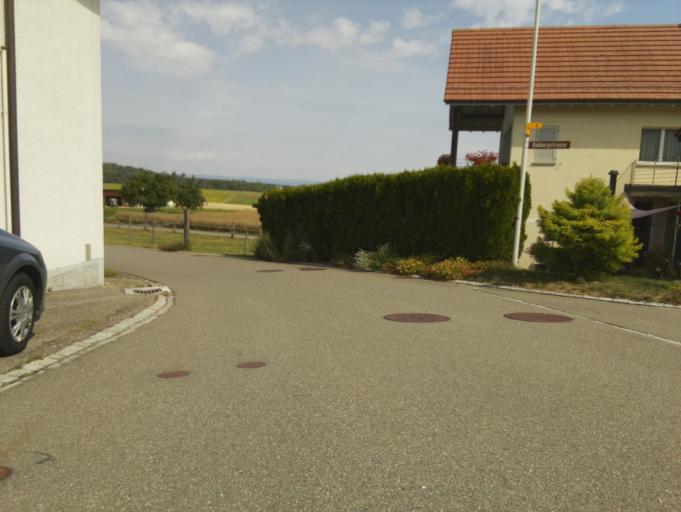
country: CH
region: Zurich
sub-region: Bezirk Andelfingen
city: Henggart
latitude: 47.5772
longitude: 8.6717
